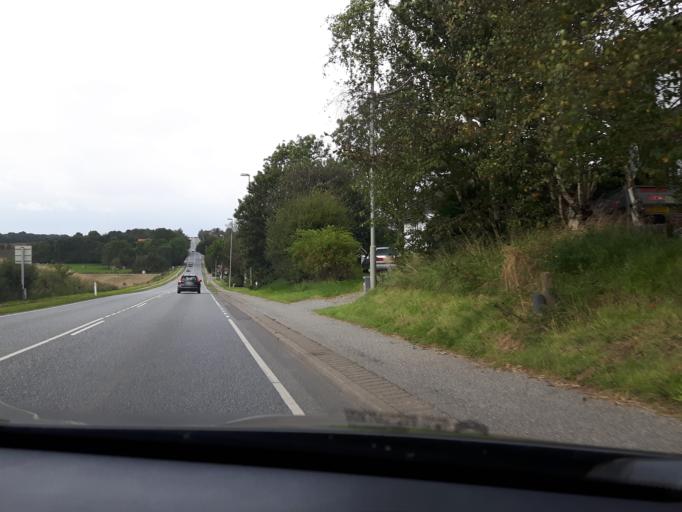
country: DK
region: North Denmark
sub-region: Jammerbugt Kommune
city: Brovst
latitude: 57.0953
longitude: 9.4857
